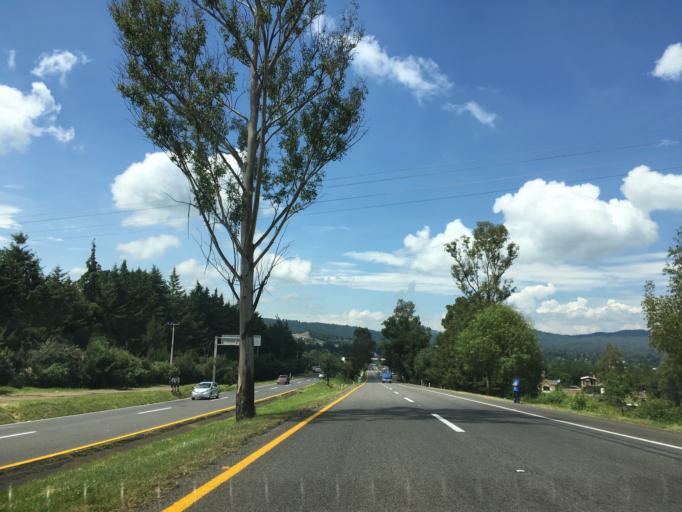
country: MX
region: Michoacan
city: Cuanajo
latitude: 19.5345
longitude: -101.5475
